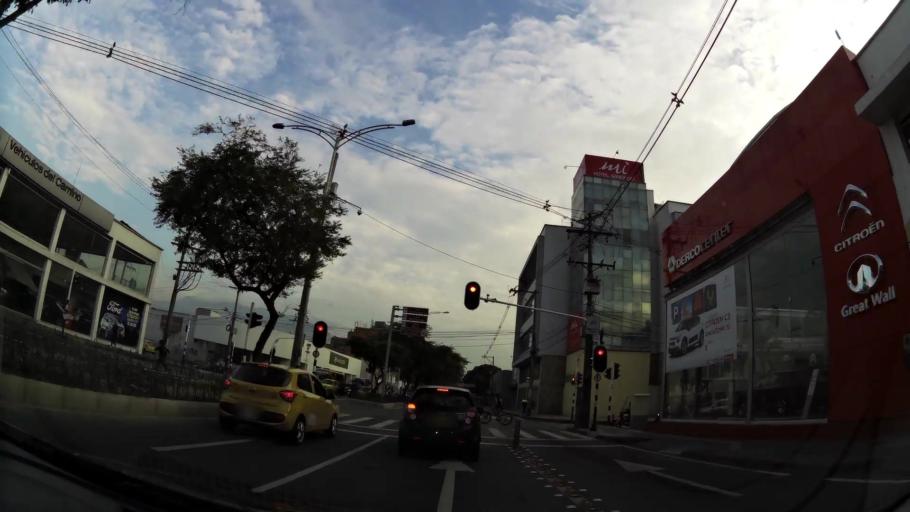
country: CO
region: Antioquia
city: Medellin
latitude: 6.2310
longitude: -75.5699
